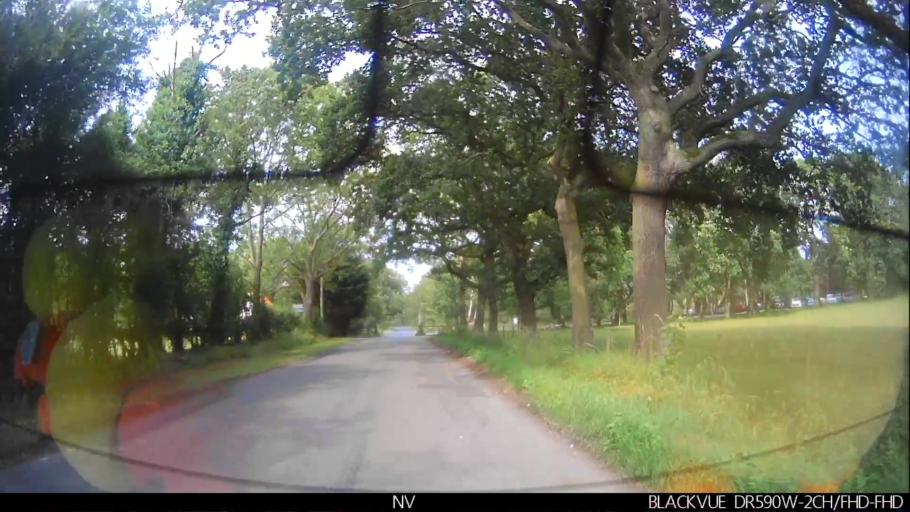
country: GB
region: England
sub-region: North Yorkshire
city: Strensall
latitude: 54.0423
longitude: -1.0123
